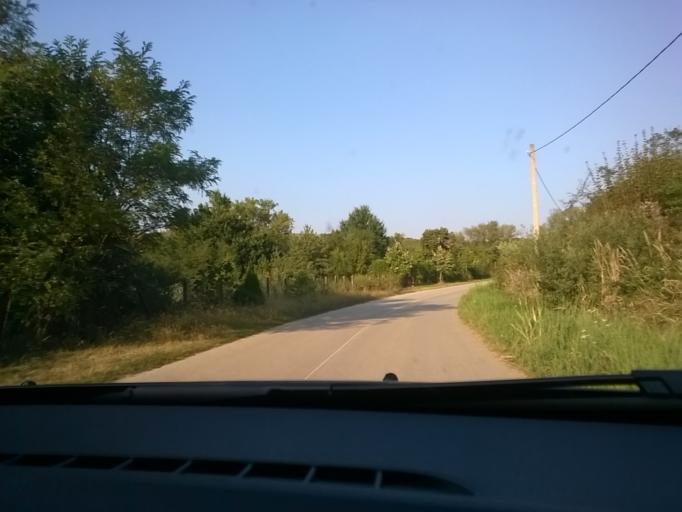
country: RS
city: Kustilj
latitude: 45.1021
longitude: 21.3843
